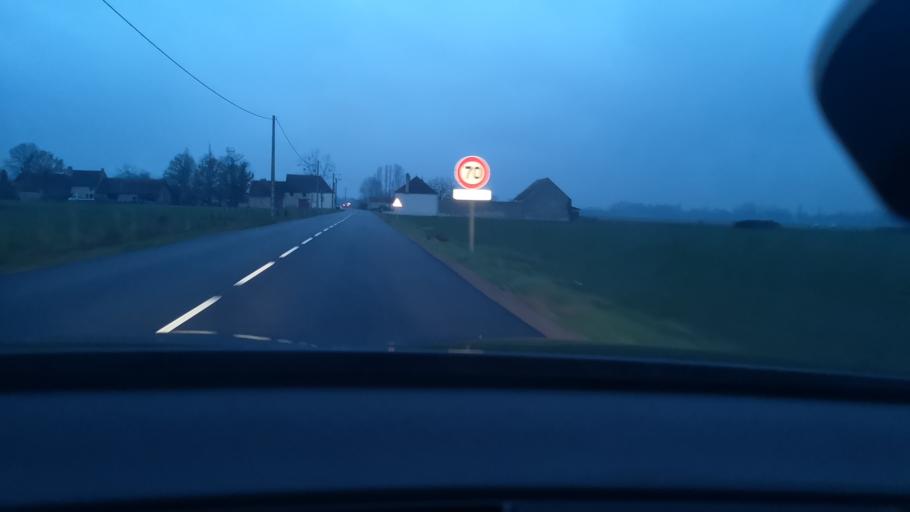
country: FR
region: Bourgogne
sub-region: Departement de Saone-et-Loire
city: Demigny
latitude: 46.9366
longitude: 4.8583
